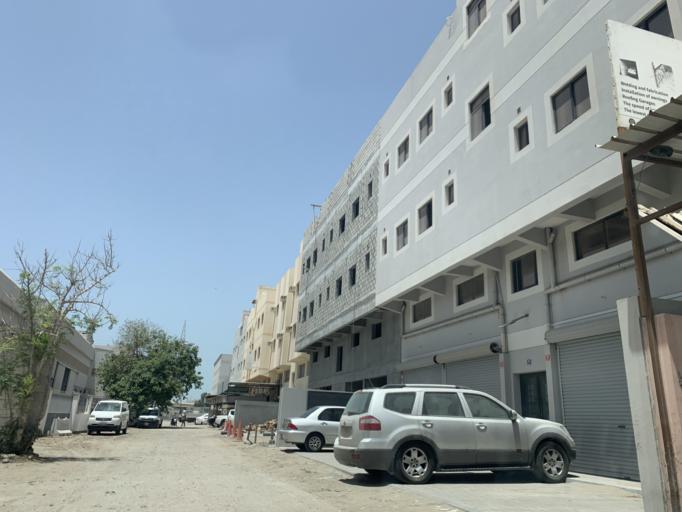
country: BH
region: Northern
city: Sitrah
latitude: 26.1755
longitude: 50.6092
